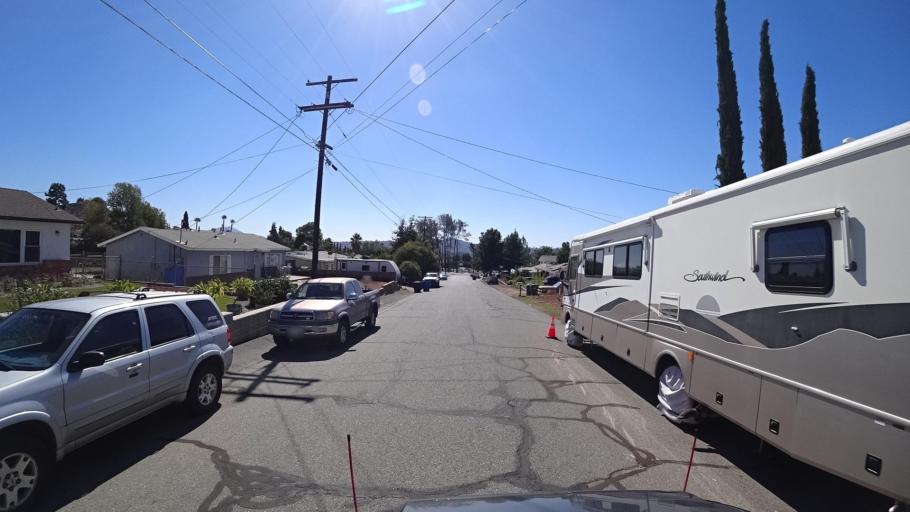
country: US
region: California
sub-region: San Diego County
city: Winter Gardens
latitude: 32.8232
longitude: -116.9452
